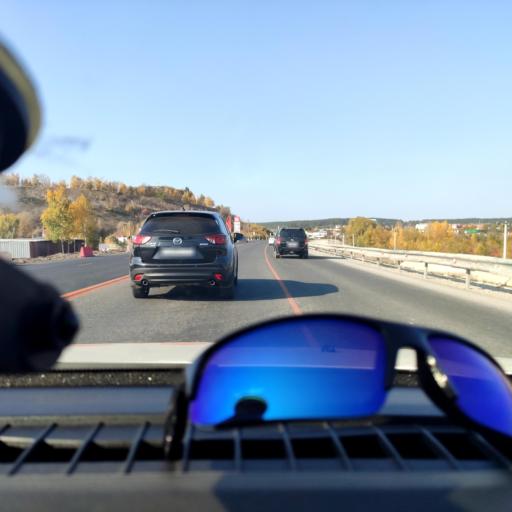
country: RU
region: Samara
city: Volzhskiy
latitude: 53.4185
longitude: 50.1280
